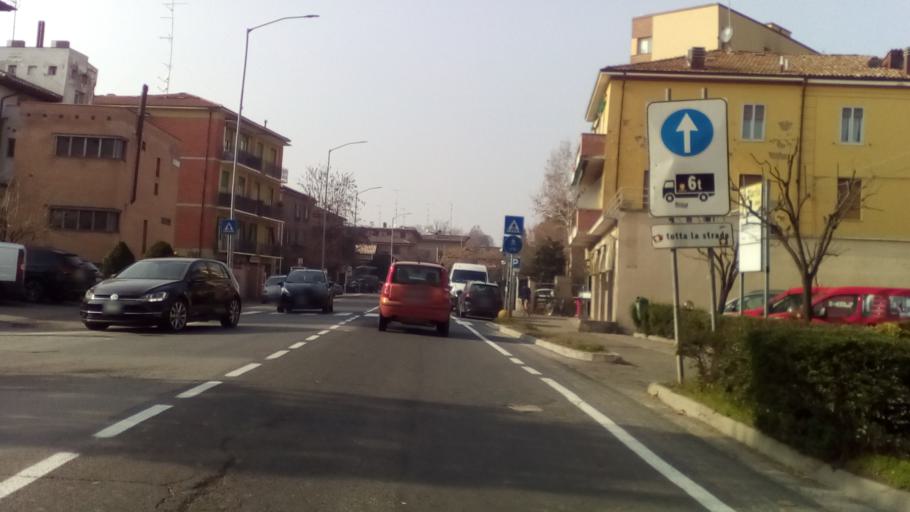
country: IT
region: Emilia-Romagna
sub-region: Provincia di Modena
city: Modena
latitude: 44.6292
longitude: 10.9441
